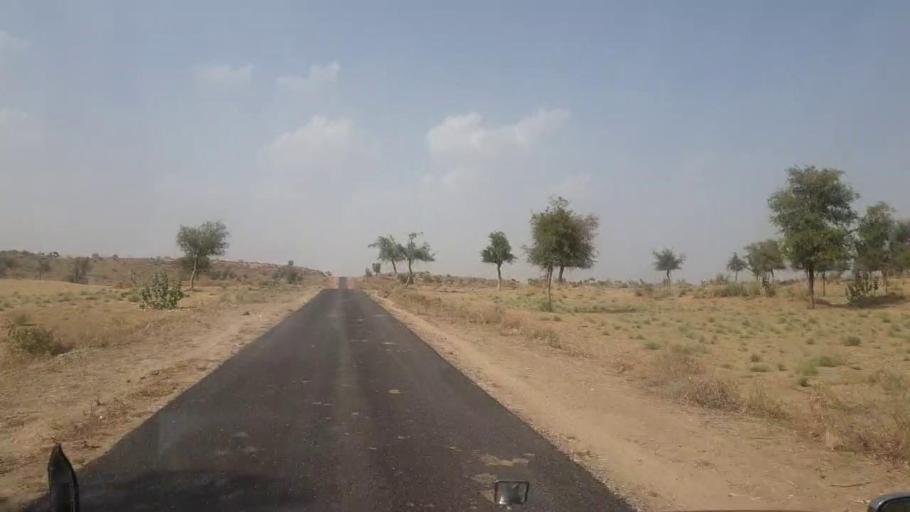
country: PK
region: Sindh
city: Islamkot
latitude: 25.1902
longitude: 70.2856
